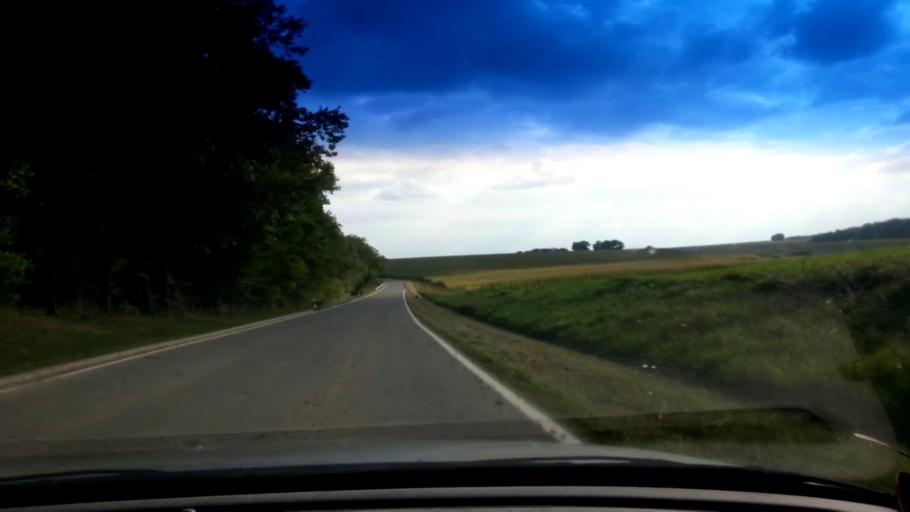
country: DE
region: Bavaria
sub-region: Upper Franconia
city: Zapfendorf
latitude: 49.9807
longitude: 10.9677
